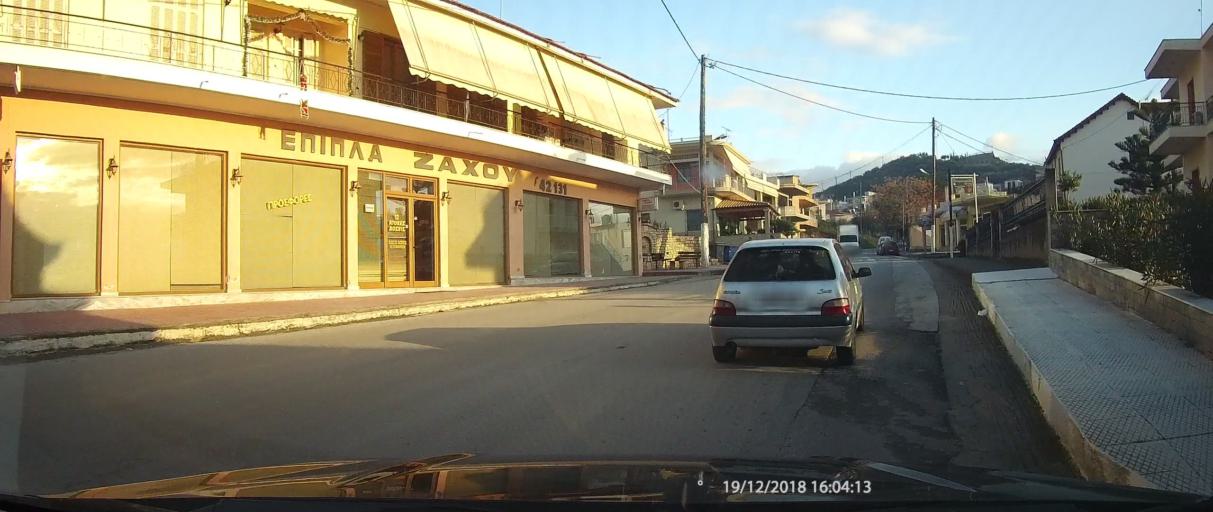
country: GR
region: Peloponnese
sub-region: Nomos Lakonias
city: Vlakhiotis
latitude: 36.8630
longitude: 22.7116
